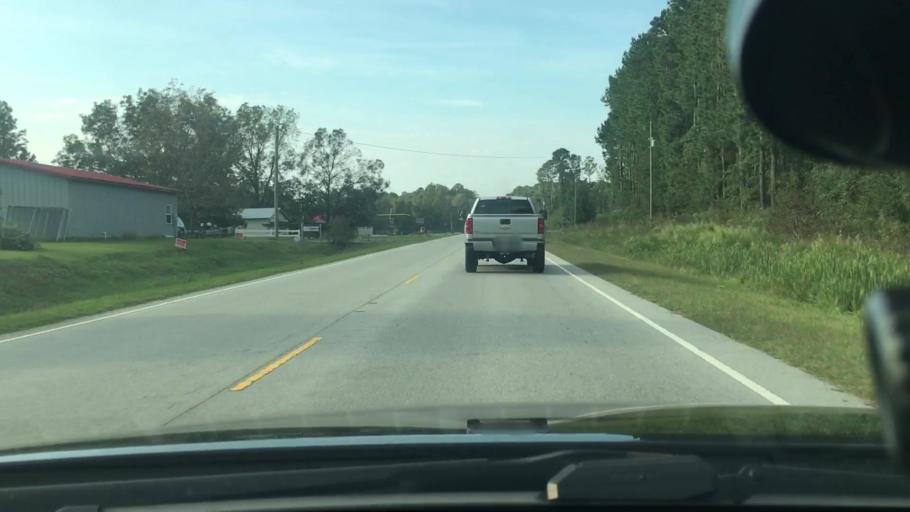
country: US
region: North Carolina
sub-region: Craven County
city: Vanceboro
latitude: 35.3153
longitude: -77.1418
